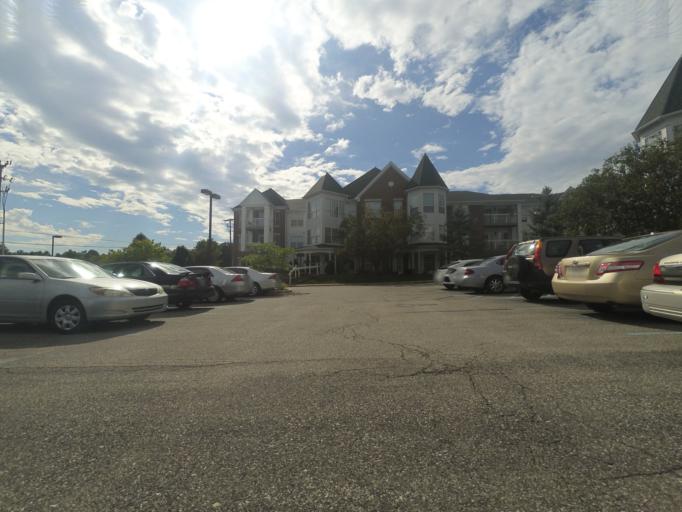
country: US
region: West Virginia
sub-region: Cabell County
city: Huntington
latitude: 38.3906
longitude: -82.4607
